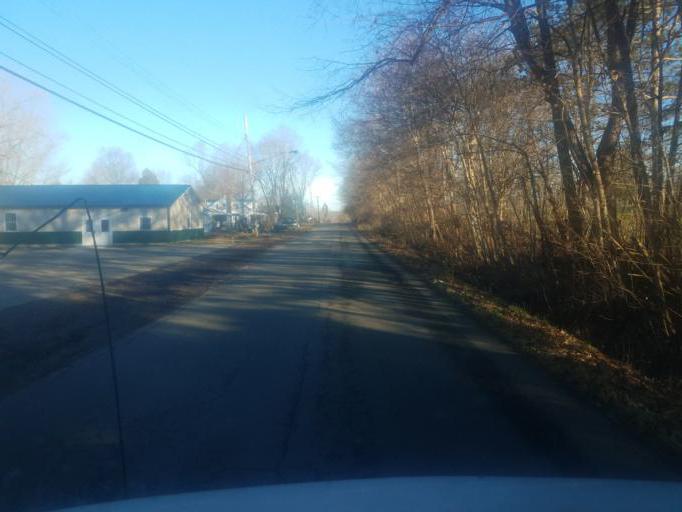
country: US
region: Ohio
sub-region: Richland County
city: Mansfield
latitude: 40.7877
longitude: -82.5357
